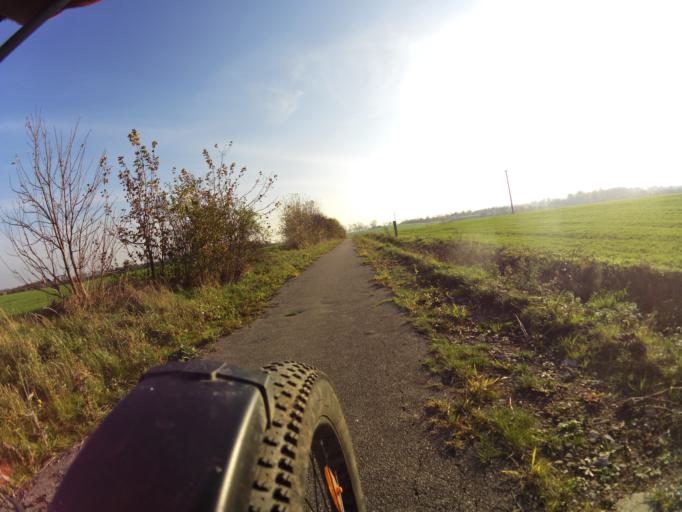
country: PL
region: Pomeranian Voivodeship
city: Strzelno
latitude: 54.7644
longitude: 18.2525
